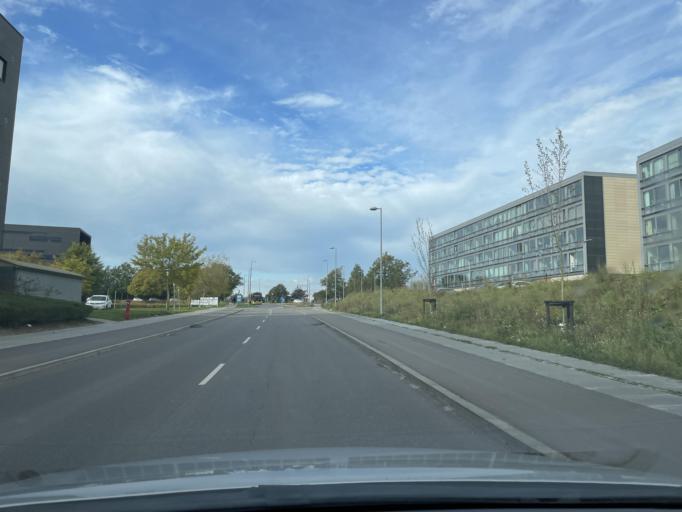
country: DK
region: Central Jutland
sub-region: Arhus Kommune
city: Stavtrup
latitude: 56.1681
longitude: 10.1559
